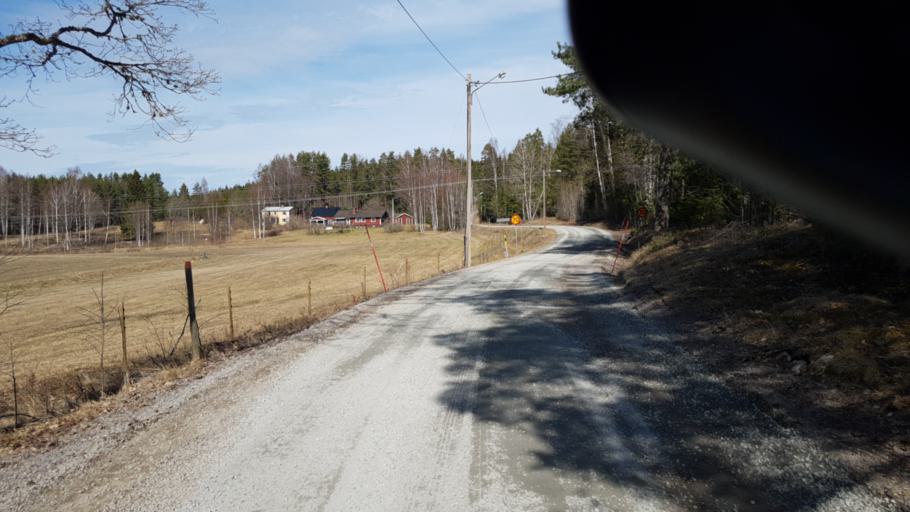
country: SE
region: Vaermland
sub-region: Grums Kommun
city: Slottsbron
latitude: 59.4562
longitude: 12.9170
